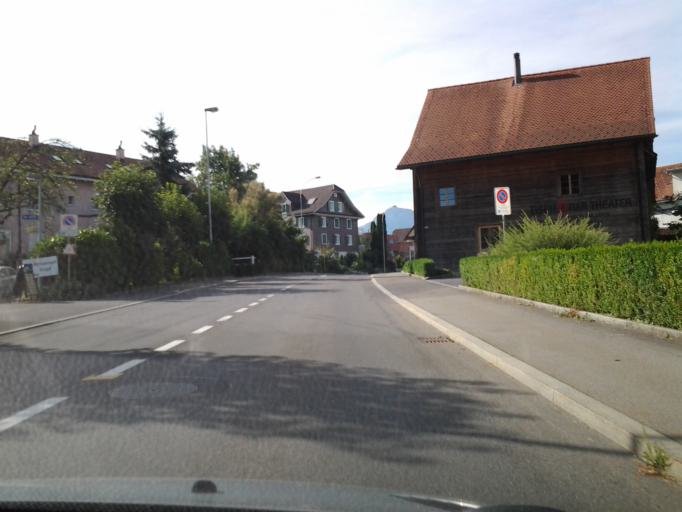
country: CH
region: Zug
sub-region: Zug
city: Hunenberg
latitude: 47.1549
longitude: 8.4399
